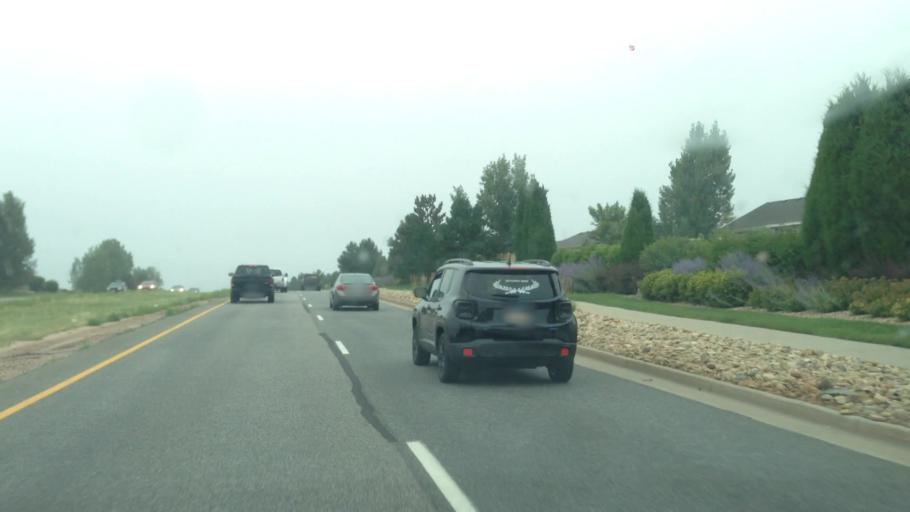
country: US
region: Colorado
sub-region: Douglas County
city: Parker
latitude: 39.6023
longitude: -104.7258
